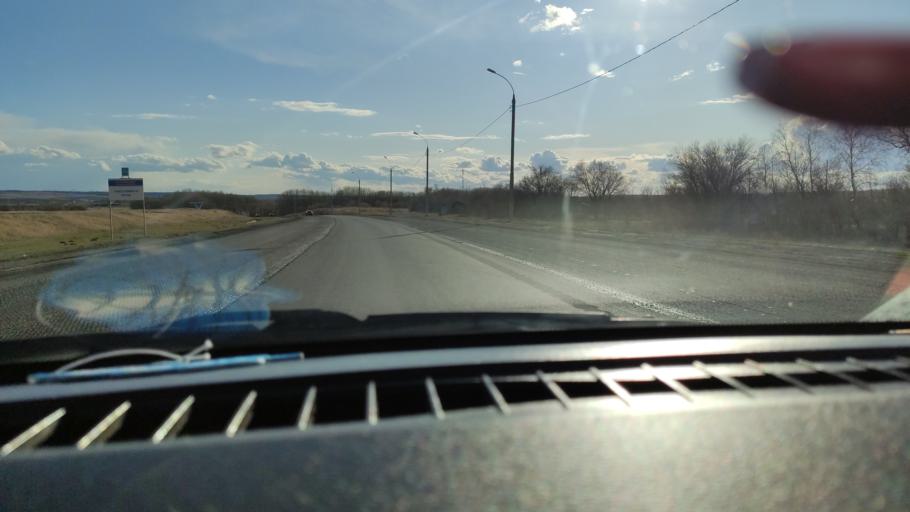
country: RU
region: Saratov
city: Yelshanka
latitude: 51.8275
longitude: 46.2236
